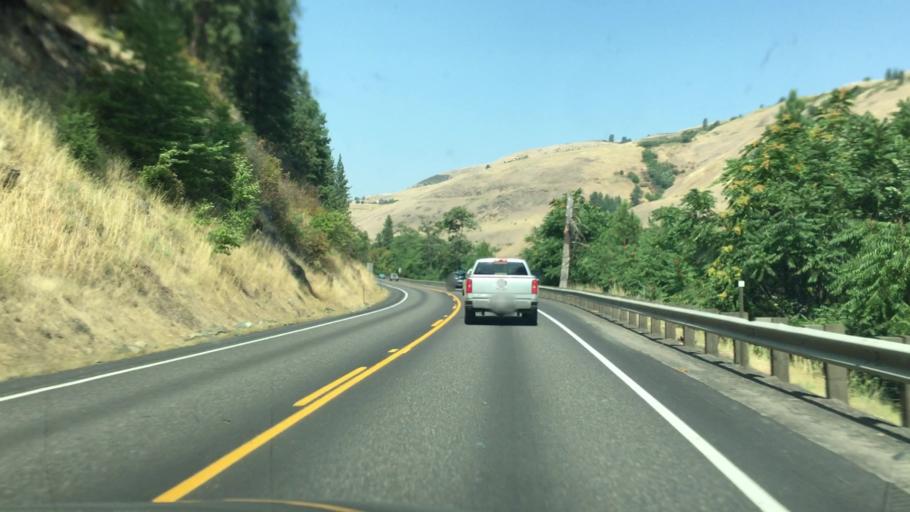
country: US
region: Idaho
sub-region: Clearwater County
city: Orofino
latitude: 46.4974
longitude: -116.4674
